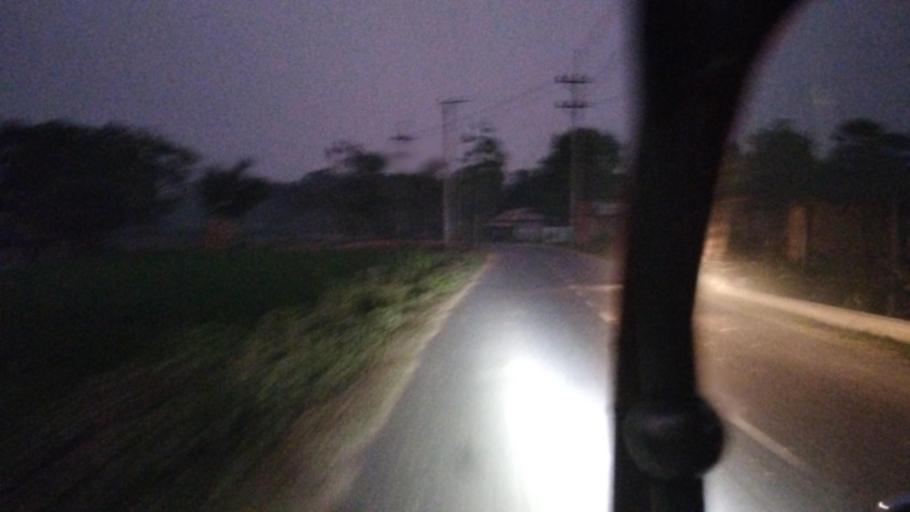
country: BD
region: Dhaka
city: Sakhipur
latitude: 24.4000
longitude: 90.3473
